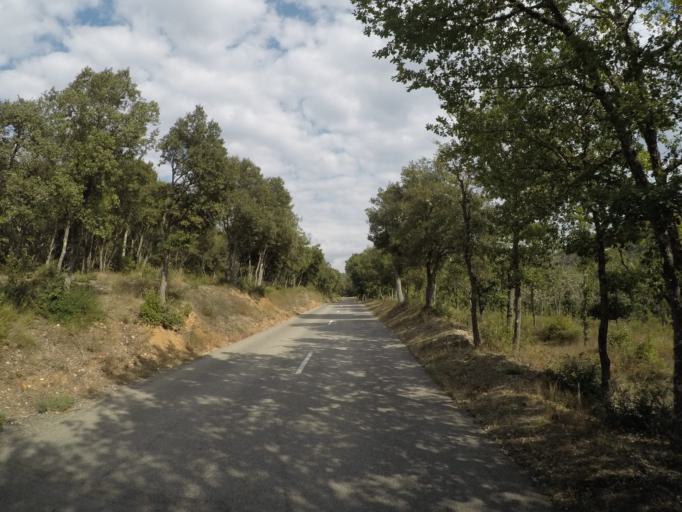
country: FR
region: Provence-Alpes-Cote d'Azur
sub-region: Departement des Alpes-de-Haute-Provence
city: Valensole
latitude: 43.8007
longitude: 5.9455
